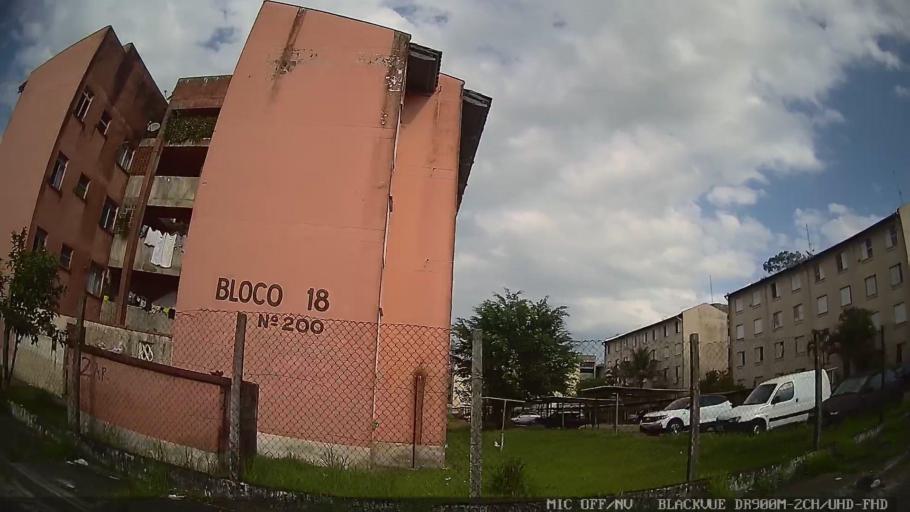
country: BR
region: Sao Paulo
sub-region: Itanhaem
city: Itanhaem
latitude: -24.1804
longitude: -46.8163
